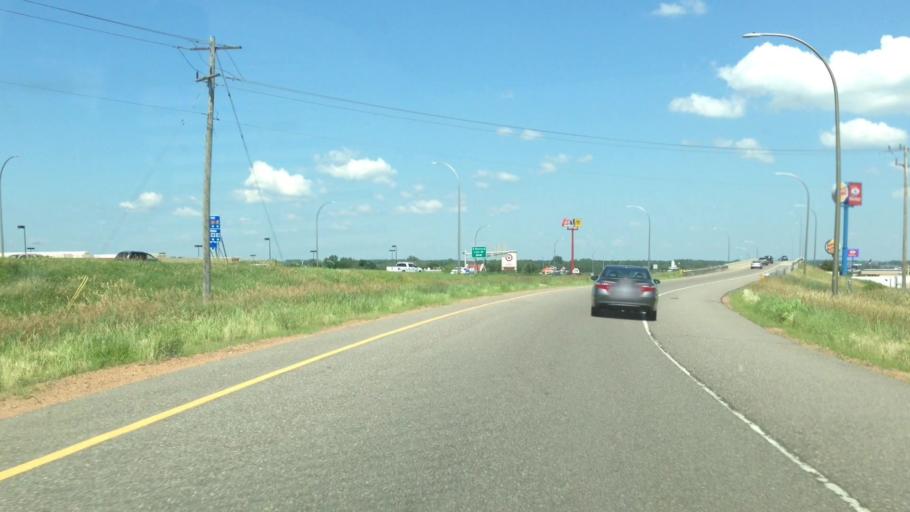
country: US
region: Minnesota
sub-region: Hennepin County
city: Rogers
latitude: 45.1962
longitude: -93.5515
